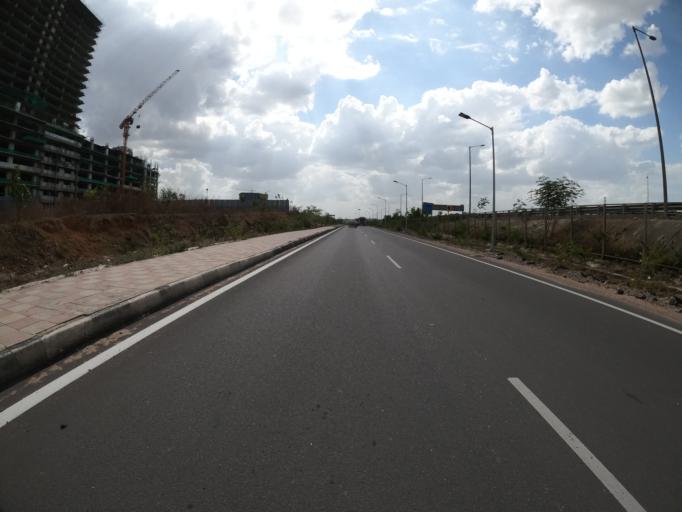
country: IN
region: Telangana
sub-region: Medak
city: Serilingampalle
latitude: 17.4051
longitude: 78.3334
